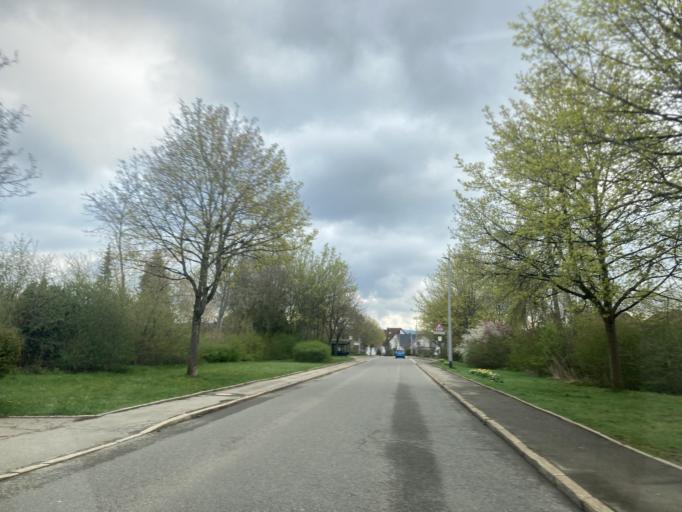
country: DE
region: Baden-Wuerttemberg
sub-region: Freiburg Region
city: Unterkirnach
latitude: 48.0311
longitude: 8.4127
